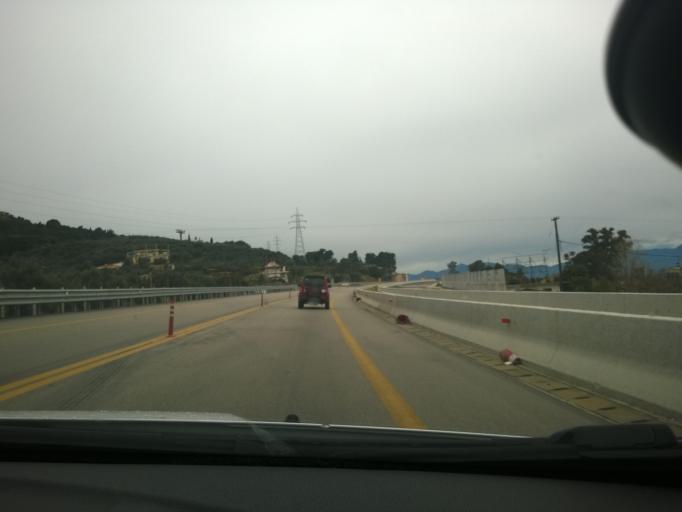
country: GR
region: West Greece
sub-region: Nomos Achaias
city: Kamarai
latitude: 38.3077
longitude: 21.9899
